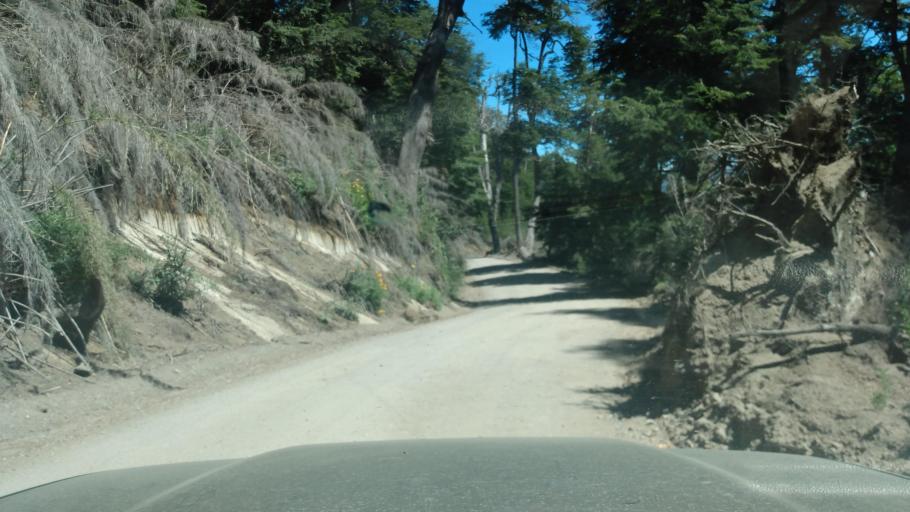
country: AR
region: Neuquen
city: Villa La Angostura
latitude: -40.6087
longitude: -71.6433
